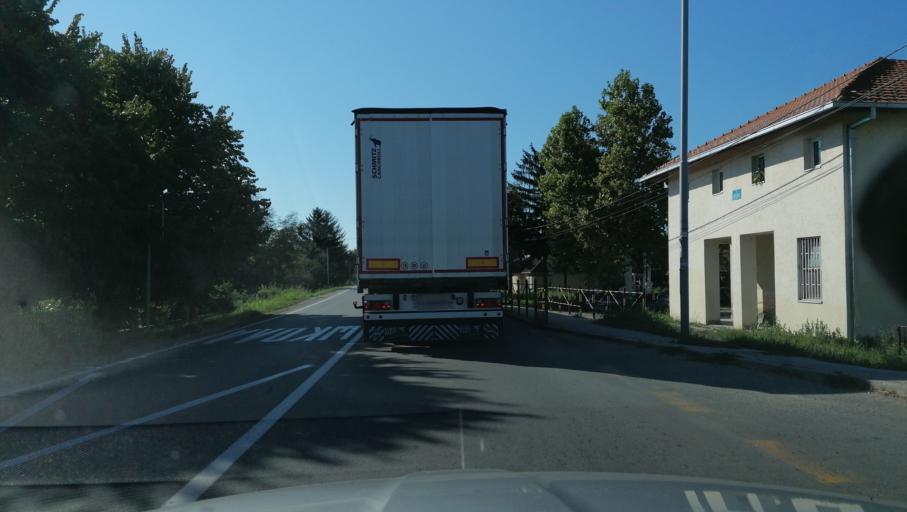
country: RS
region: Central Serbia
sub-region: Raski Okrug
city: Kraljevo
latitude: 43.7569
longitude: 20.6558
